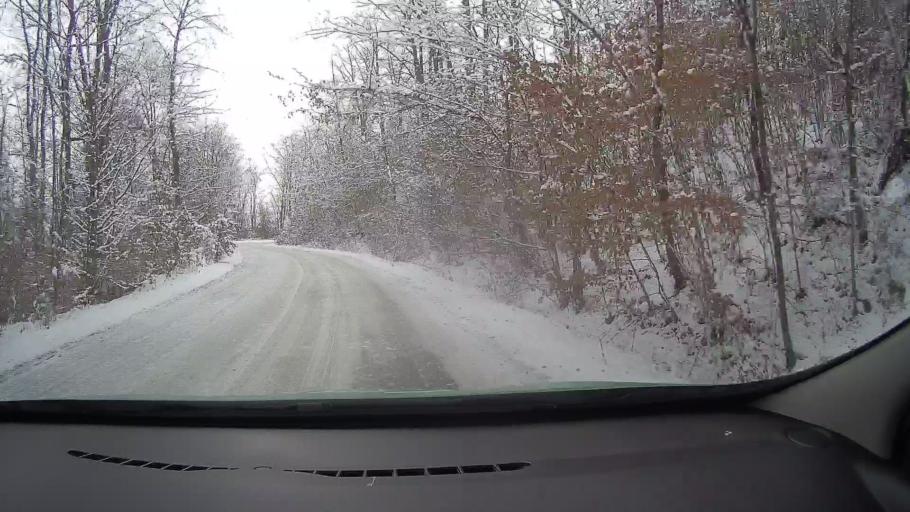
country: RO
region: Alba
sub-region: Comuna Almasu Mare
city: Almasu Mare
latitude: 46.0971
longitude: 23.1712
